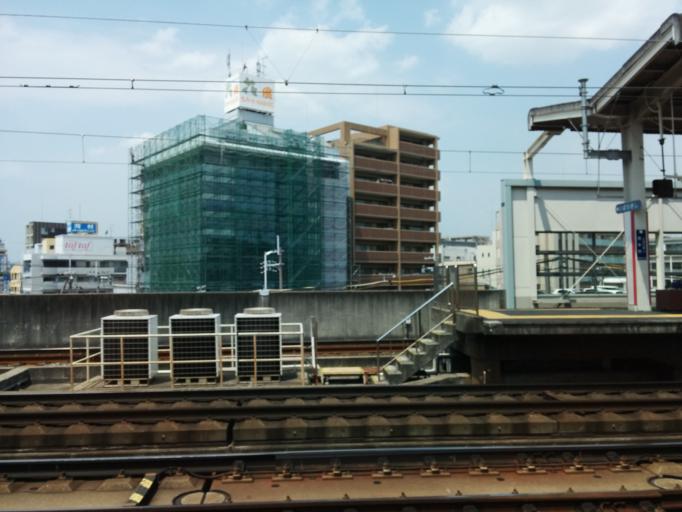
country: JP
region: Osaka
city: Ibaraki
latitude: 34.8159
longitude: 135.5753
